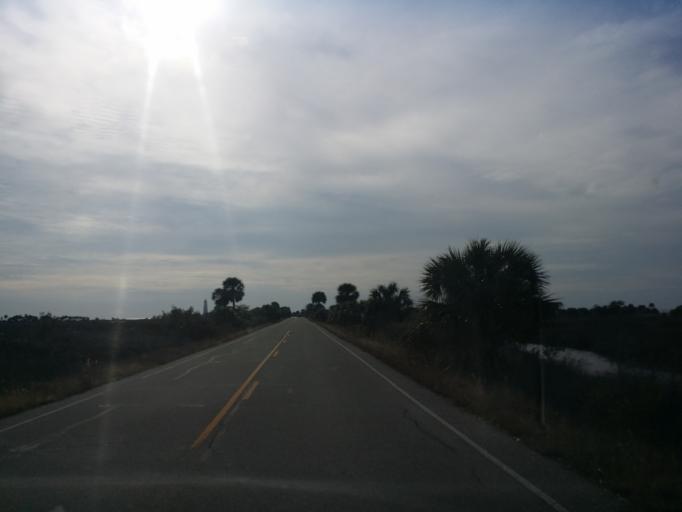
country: US
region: Florida
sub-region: Wakulla County
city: Crawfordville
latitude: 30.0799
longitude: -84.1743
